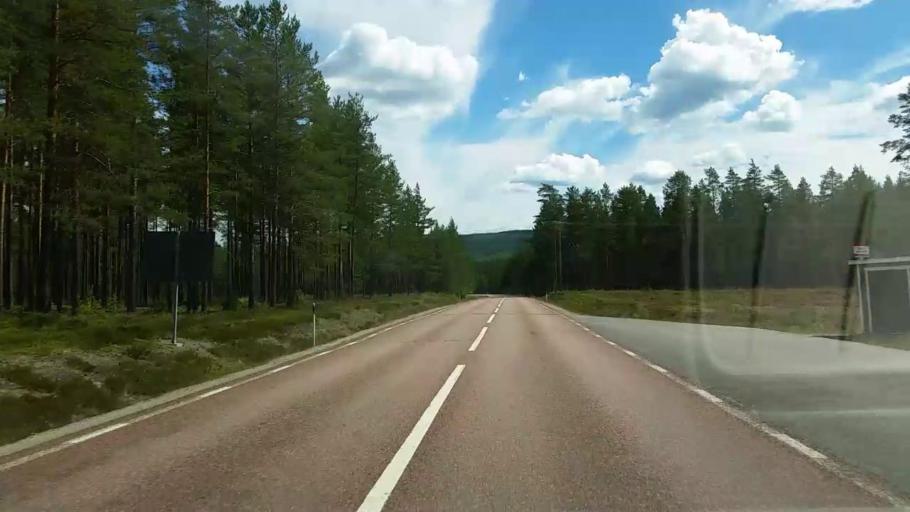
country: SE
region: Gaevleborg
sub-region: Ovanakers Kommun
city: Edsbyn
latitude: 61.3497
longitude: 15.5901
